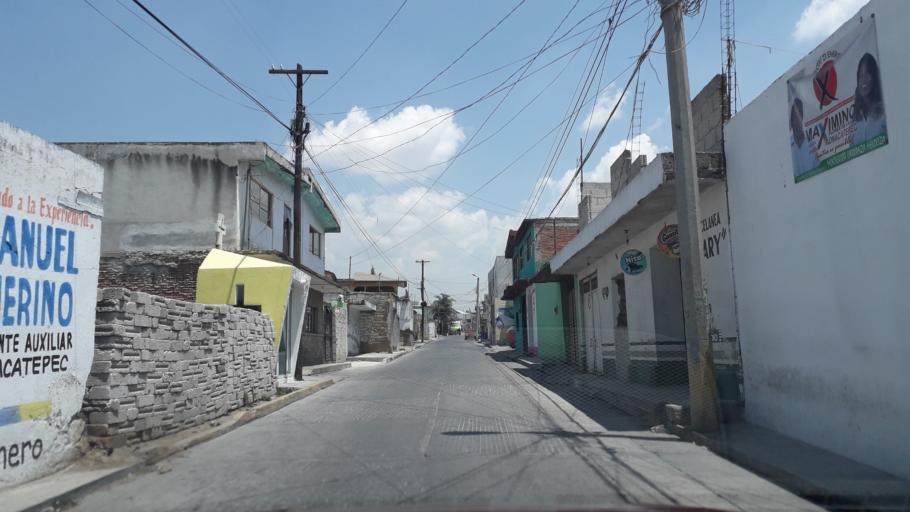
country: MX
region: Puebla
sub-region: Puebla
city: Santa Maria Xonacatepec
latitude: 19.0873
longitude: -98.1022
